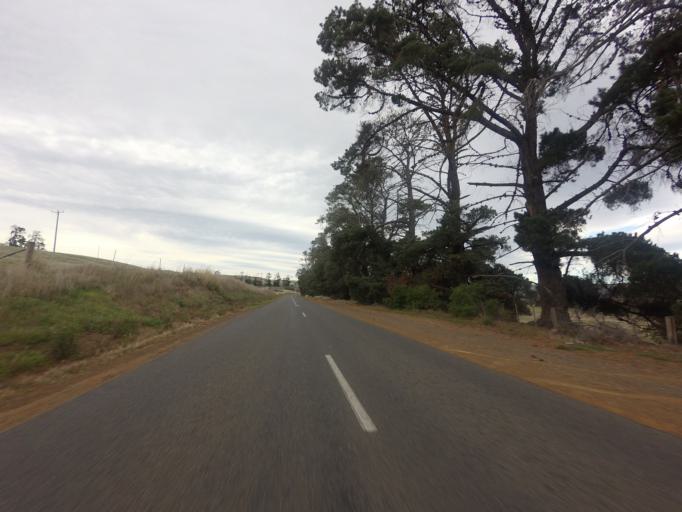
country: AU
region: Tasmania
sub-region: Derwent Valley
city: New Norfolk
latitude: -42.5164
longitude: 146.7464
